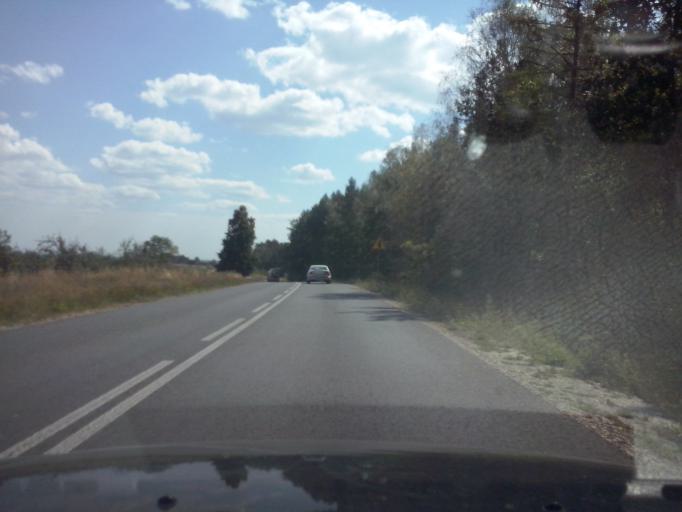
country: PL
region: Swietokrzyskie
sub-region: Powiat staszowski
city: Szydlow
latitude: 50.5832
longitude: 21.0614
